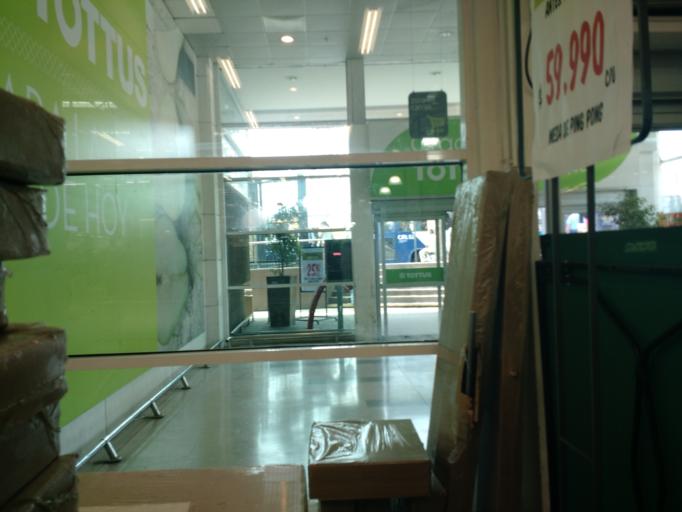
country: CL
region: Santiago Metropolitan
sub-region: Provincia de Maipo
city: San Bernardo
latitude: -33.5538
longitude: -70.6751
